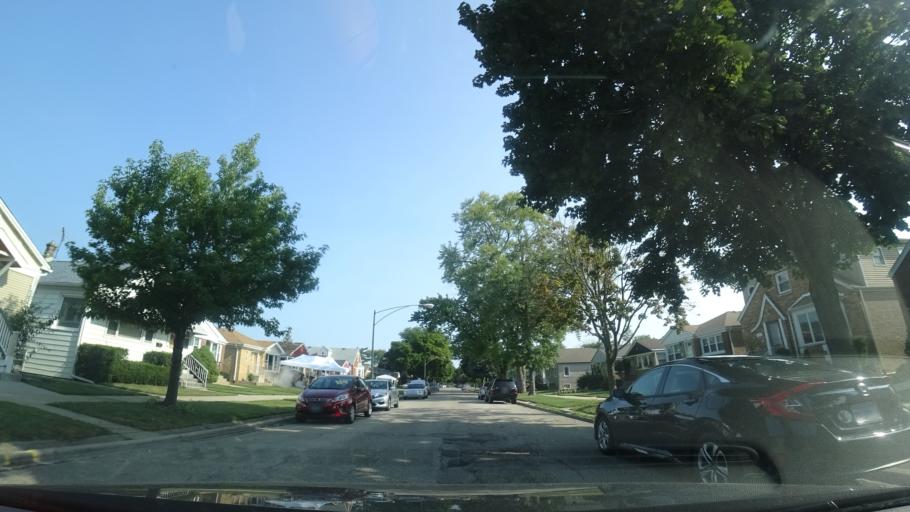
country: US
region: Illinois
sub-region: Cook County
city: Harwood Heights
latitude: 41.9762
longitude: -87.7823
